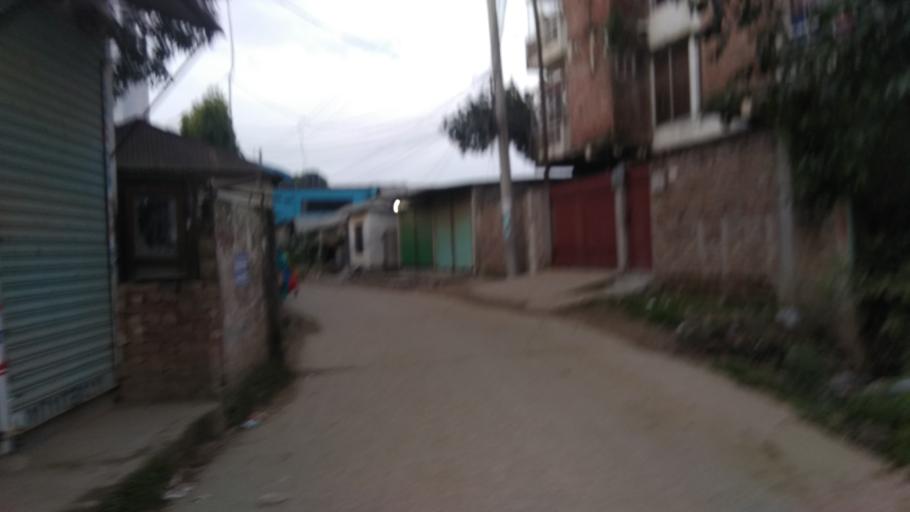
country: BD
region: Dhaka
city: Tungi
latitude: 23.8511
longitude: 90.4253
